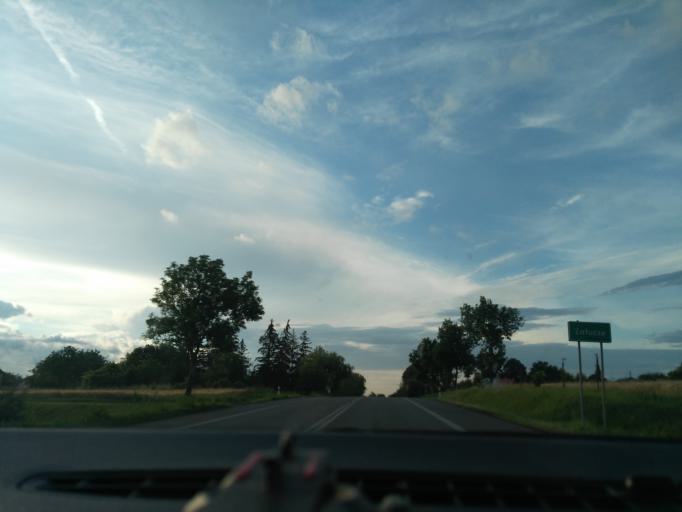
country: PL
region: Lublin Voivodeship
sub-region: Powiat lubelski
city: Niedrzwica Duza
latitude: 51.0731
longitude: 22.3766
